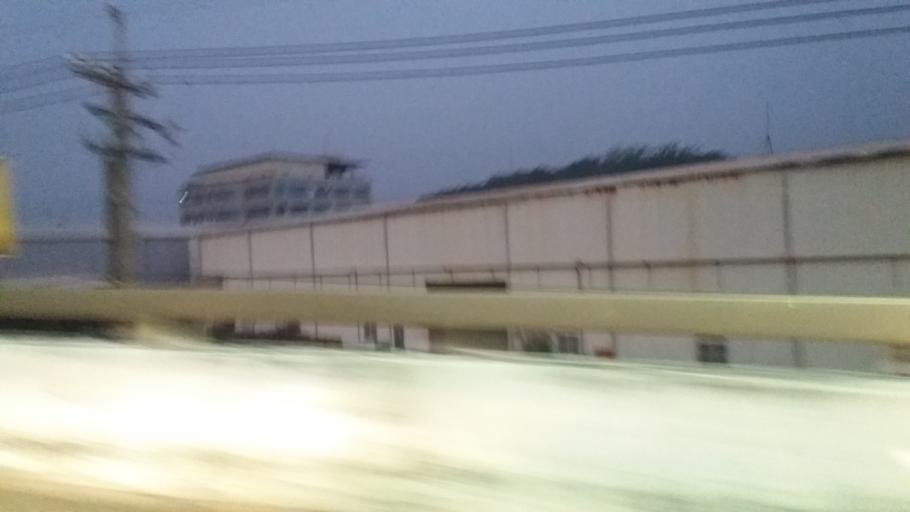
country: TW
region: Taiwan
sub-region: Hsinchu
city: Hsinchu
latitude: 24.7543
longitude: 120.9109
